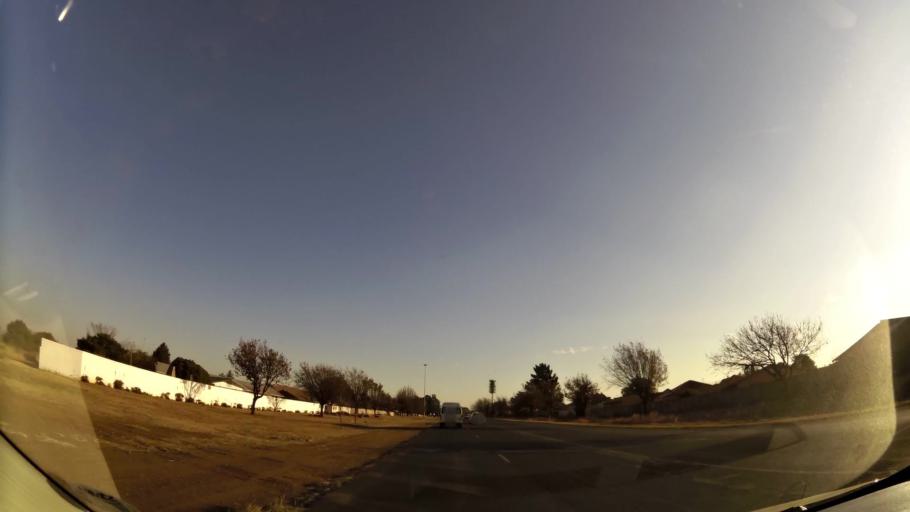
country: ZA
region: Gauteng
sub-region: West Rand District Municipality
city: Randfontein
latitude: -26.2080
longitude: 27.6586
